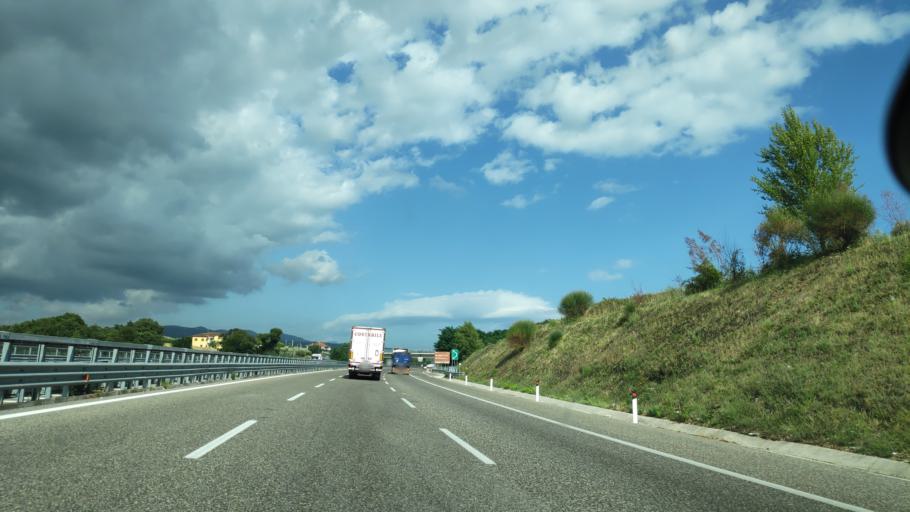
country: IT
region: Campania
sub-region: Provincia di Salerno
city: Contursi Terme
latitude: 40.6150
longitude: 15.2717
